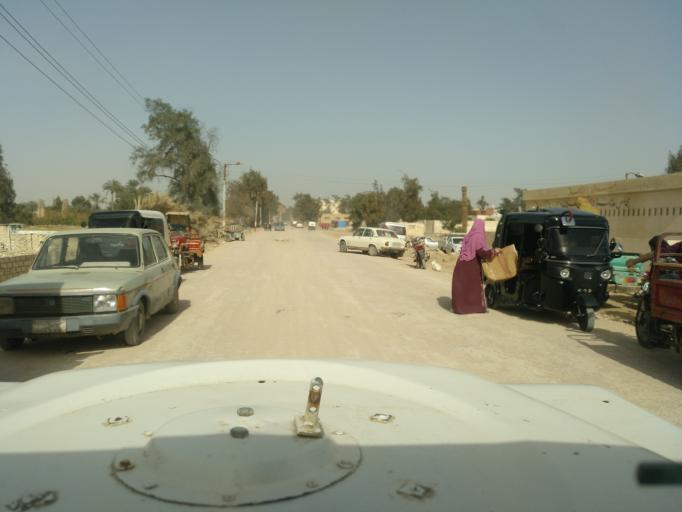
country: EG
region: Al Buhayrah
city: Beheira
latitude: 30.3684
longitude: 30.3587
